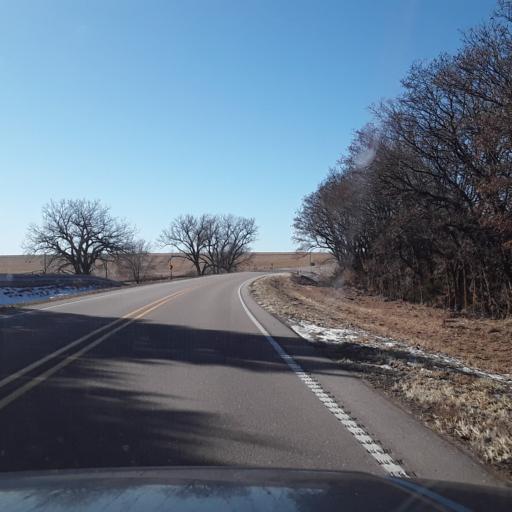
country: US
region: Nebraska
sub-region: Frontier County
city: Stockville
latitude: 40.7015
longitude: -100.2537
